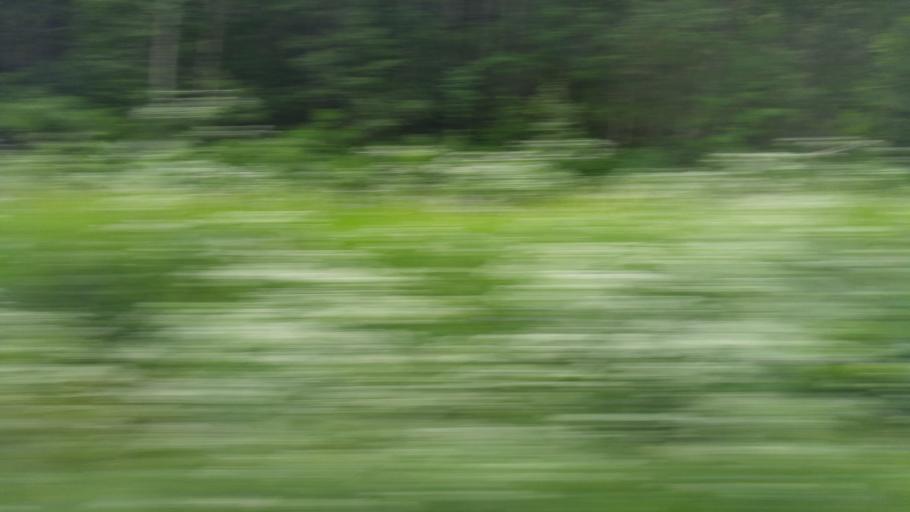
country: NO
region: Nord-Trondelag
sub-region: Levanger
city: Levanger
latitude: 63.4578
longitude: 11.3680
